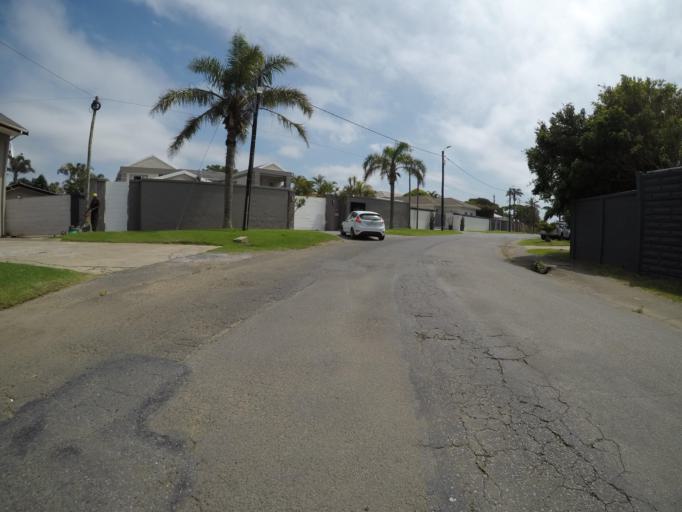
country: ZA
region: Eastern Cape
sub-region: Buffalo City Metropolitan Municipality
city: East London
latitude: -32.9400
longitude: 28.0221
